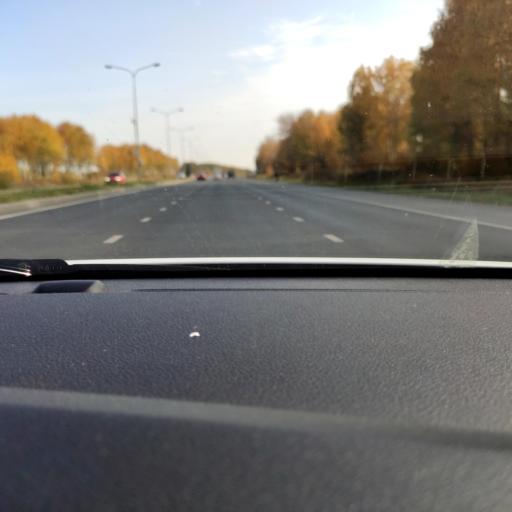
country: RU
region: Tatarstan
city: Vysokaya Gora
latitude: 55.8015
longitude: 49.3132
